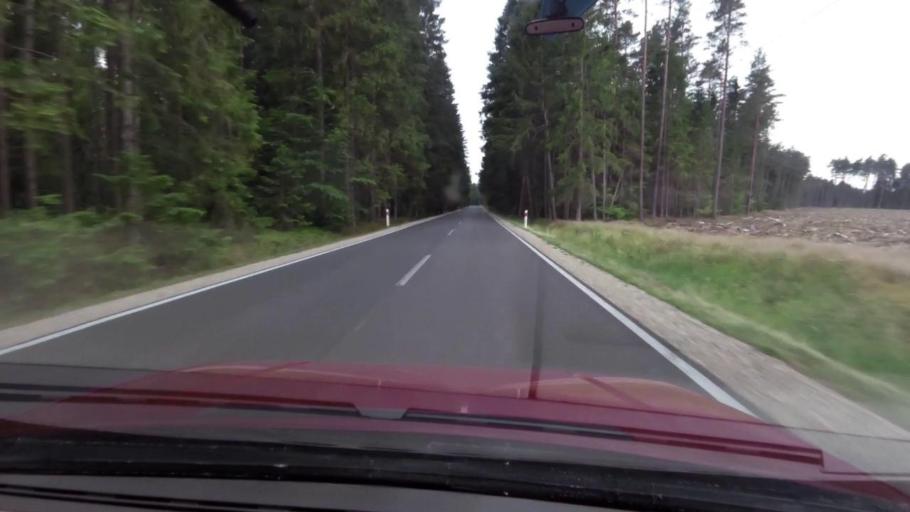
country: PL
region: West Pomeranian Voivodeship
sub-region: Powiat koszalinski
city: Polanow
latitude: 54.1437
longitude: 16.4840
